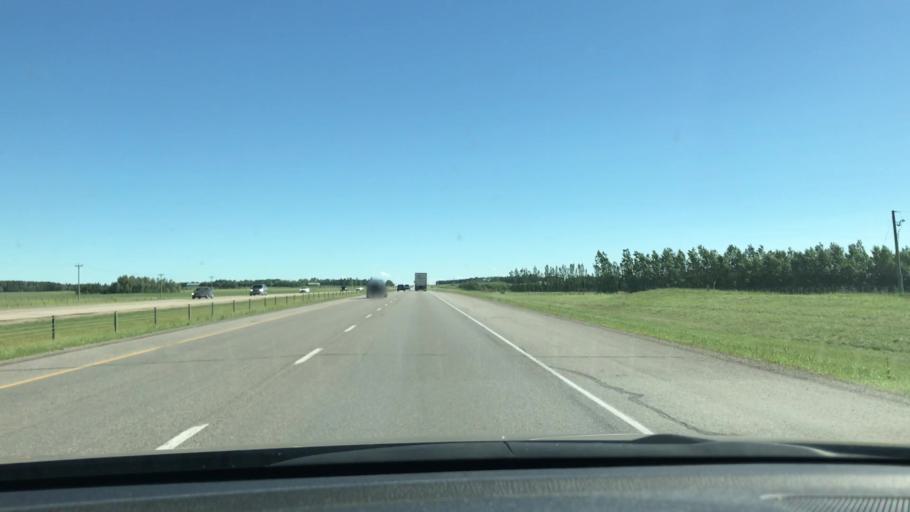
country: CA
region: Alberta
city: Olds
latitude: 51.9041
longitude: -114.0250
